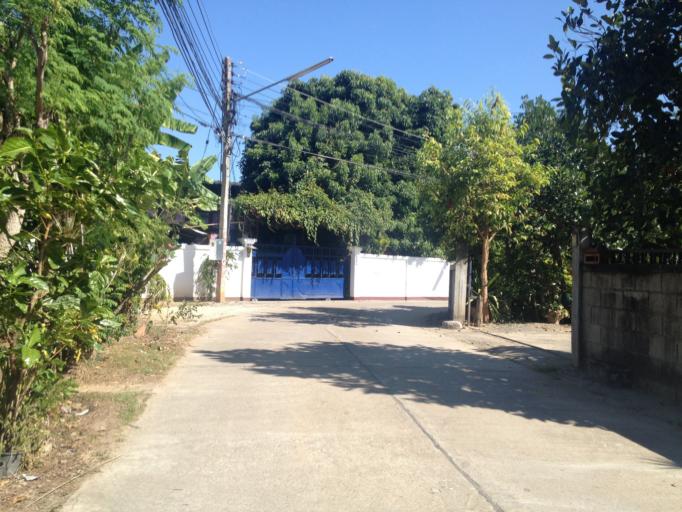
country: TH
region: Chiang Mai
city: Hang Dong
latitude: 18.6966
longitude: 98.9297
